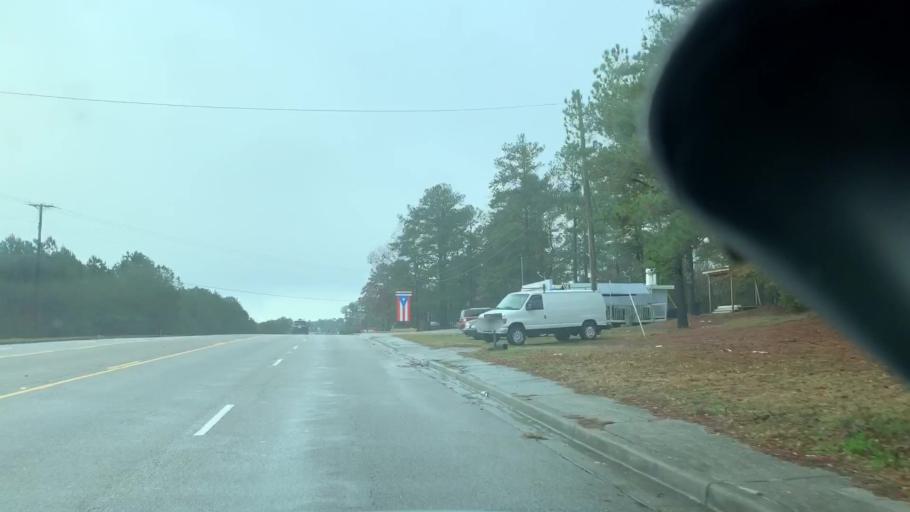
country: US
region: South Carolina
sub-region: Richland County
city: Woodfield
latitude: 34.0486
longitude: -80.9283
